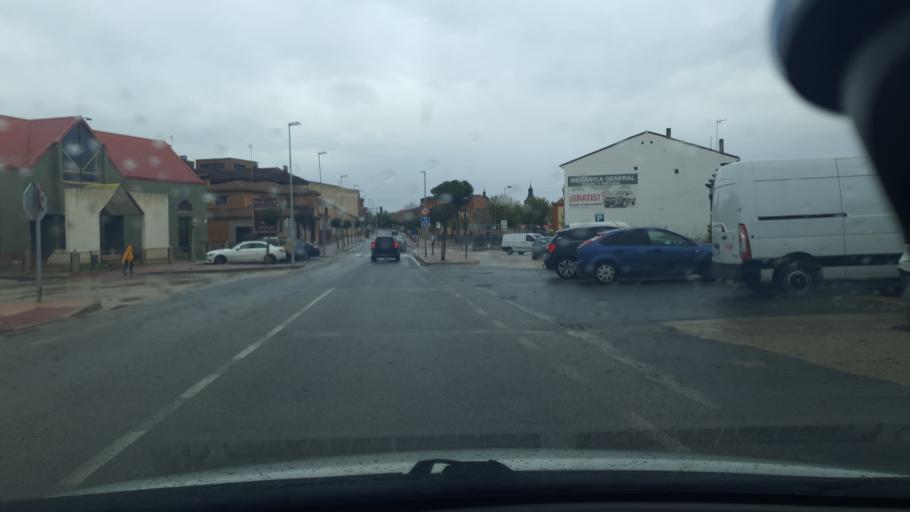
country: ES
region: Castille and Leon
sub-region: Provincia de Segovia
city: Carbonero el Mayor
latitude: 41.1179
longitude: -4.2637
